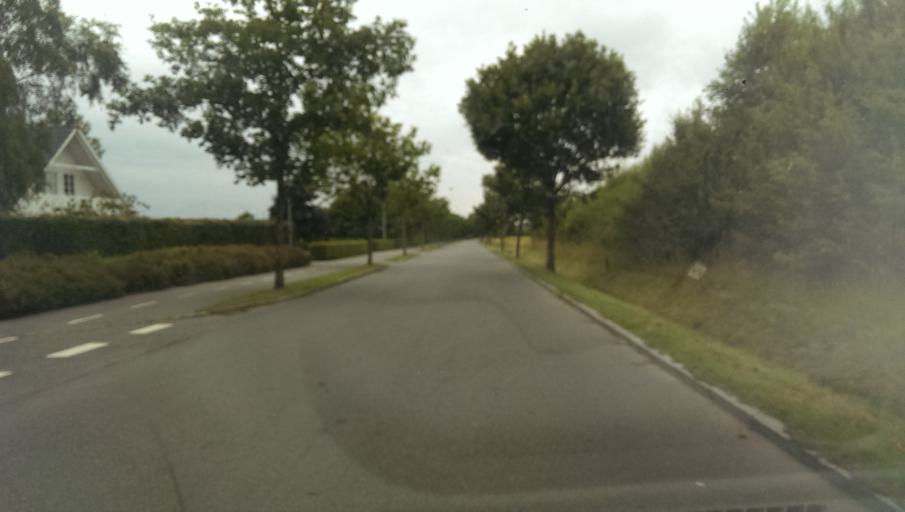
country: DK
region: South Denmark
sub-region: Esbjerg Kommune
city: Bramming
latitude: 55.4737
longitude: 8.7152
